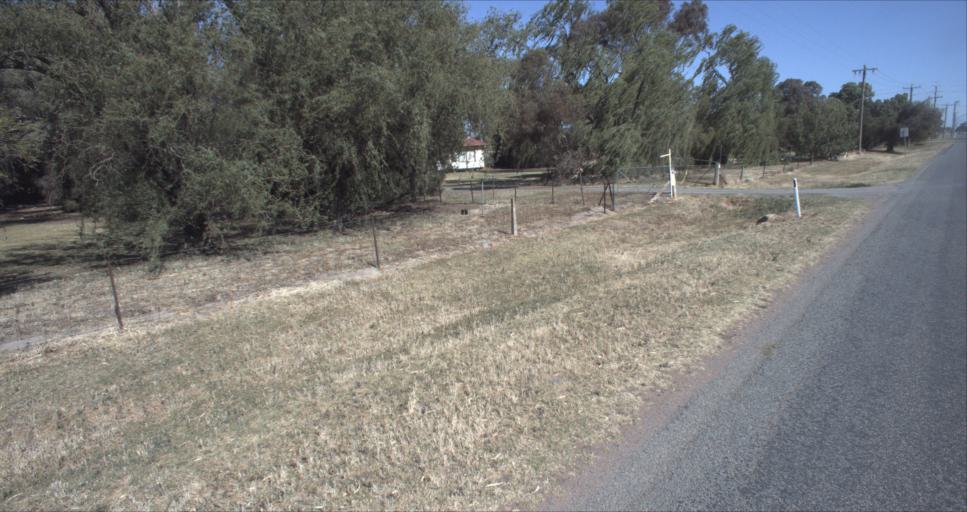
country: AU
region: New South Wales
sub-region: Leeton
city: Leeton
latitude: -34.5423
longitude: 146.4188
